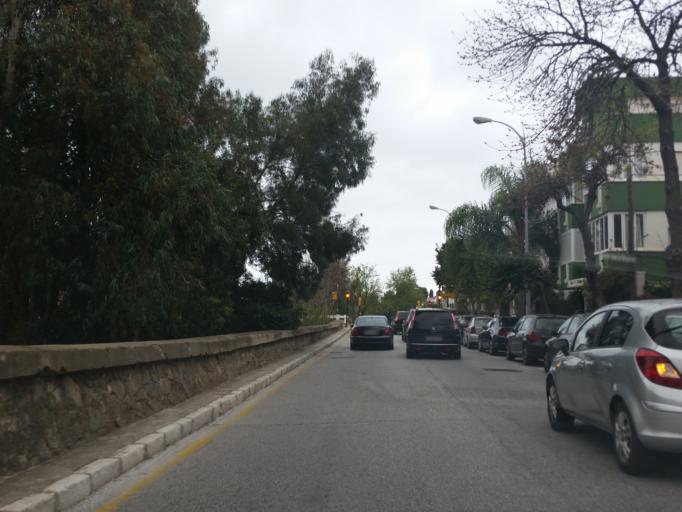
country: ES
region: Andalusia
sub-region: Provincia de Malaga
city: Malaga
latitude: 36.7230
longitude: -4.3663
